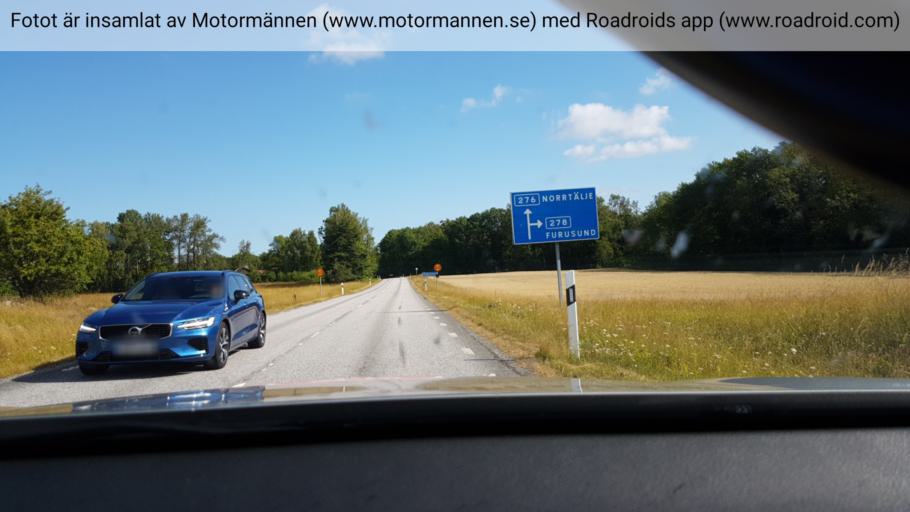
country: SE
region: Stockholm
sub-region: Norrtalje Kommun
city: Norrtalje
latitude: 59.6755
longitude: 18.6814
